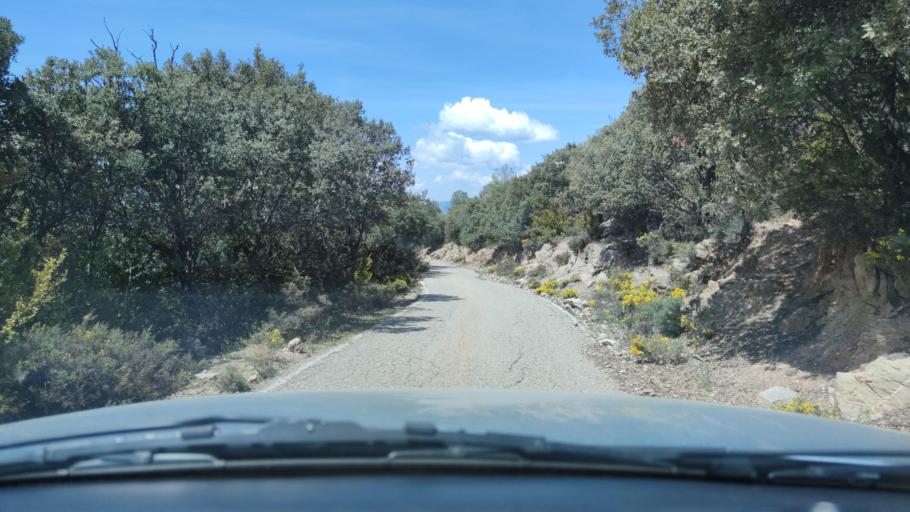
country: ES
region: Catalonia
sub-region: Provincia de Lleida
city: Sort
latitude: 42.3078
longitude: 1.1145
